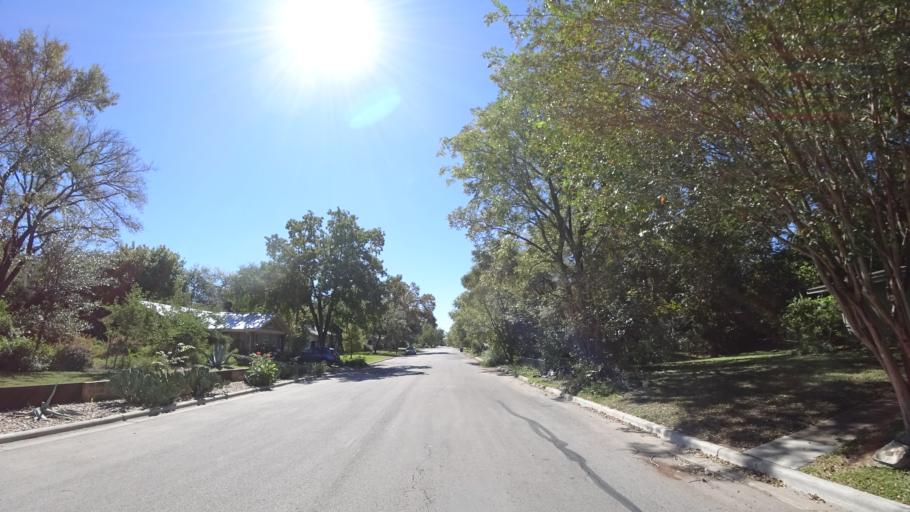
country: US
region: Texas
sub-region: Travis County
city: West Lake Hills
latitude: 30.3372
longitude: -97.7444
